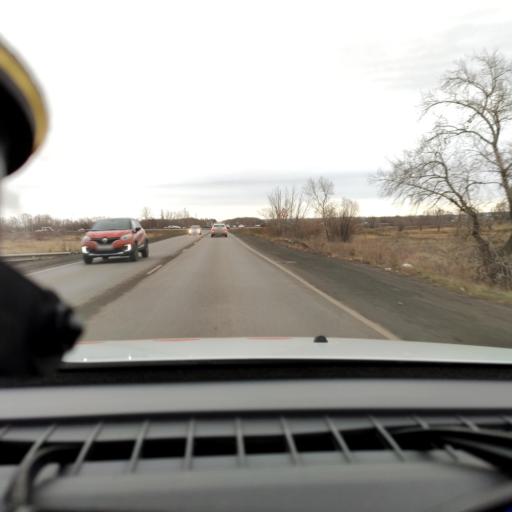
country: RU
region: Samara
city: Samara
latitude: 53.0944
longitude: 50.1480
